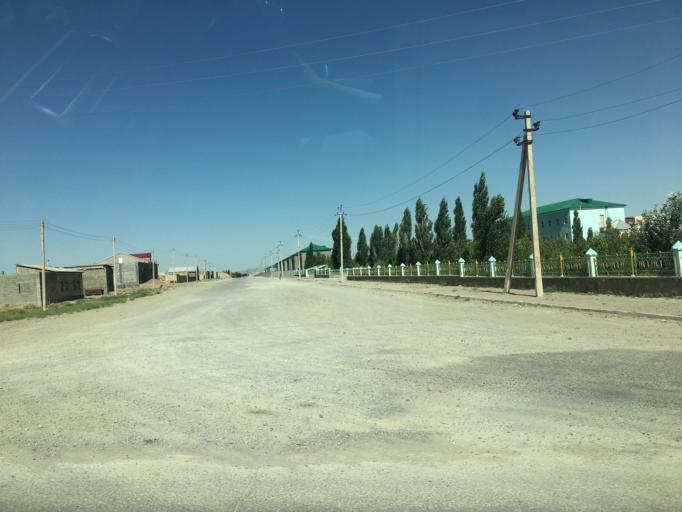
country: TM
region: Balkan
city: Serdar
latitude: 38.9688
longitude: 56.2953
